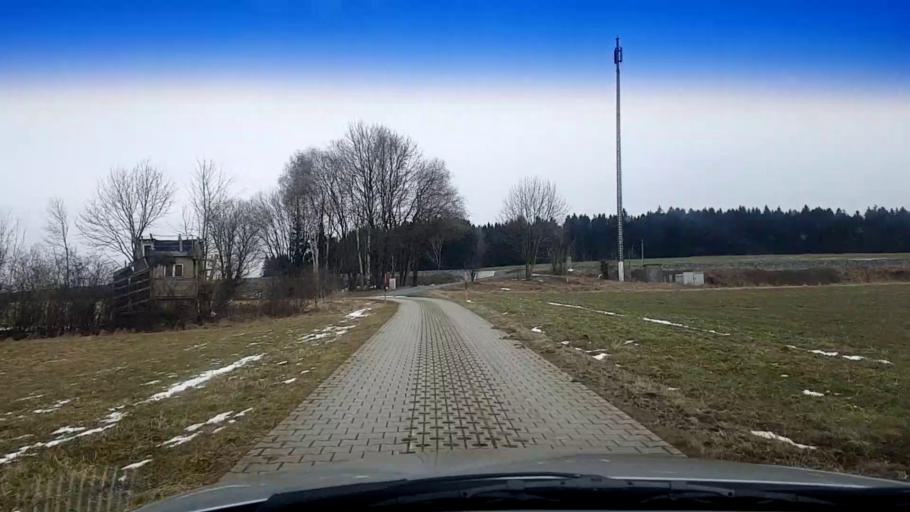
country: DE
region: Bavaria
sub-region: Upper Franconia
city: Stammbach
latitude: 50.1670
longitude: 11.7037
